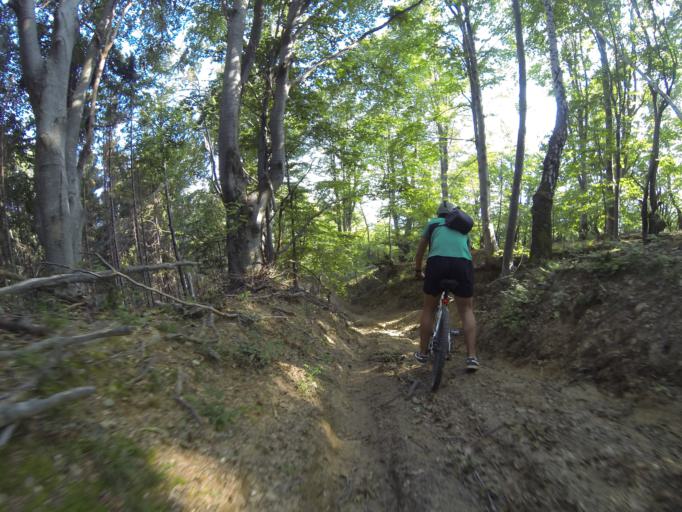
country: RO
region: Valcea
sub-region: Comuna Vaideeni
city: Vaideeni
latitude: 45.2159
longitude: 23.9724
